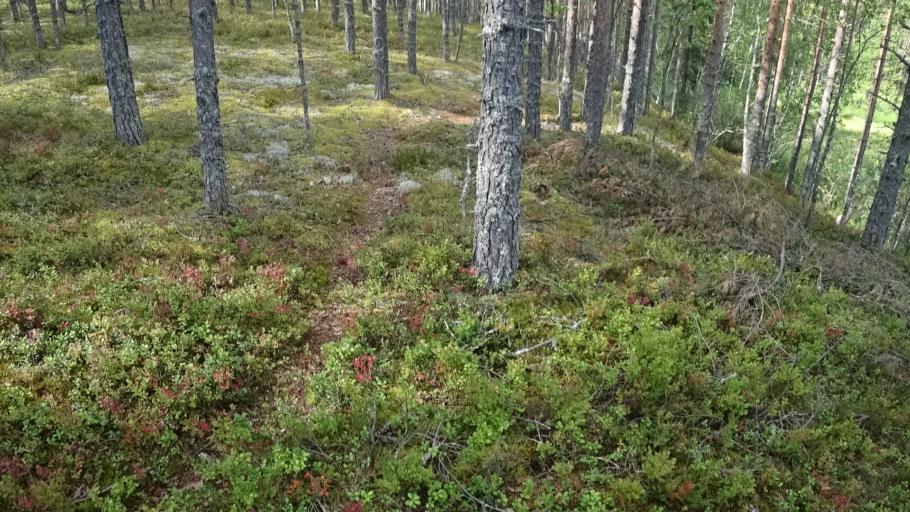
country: FI
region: North Karelia
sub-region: Joensuu
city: Ilomantsi
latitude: 62.6083
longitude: 31.1872
